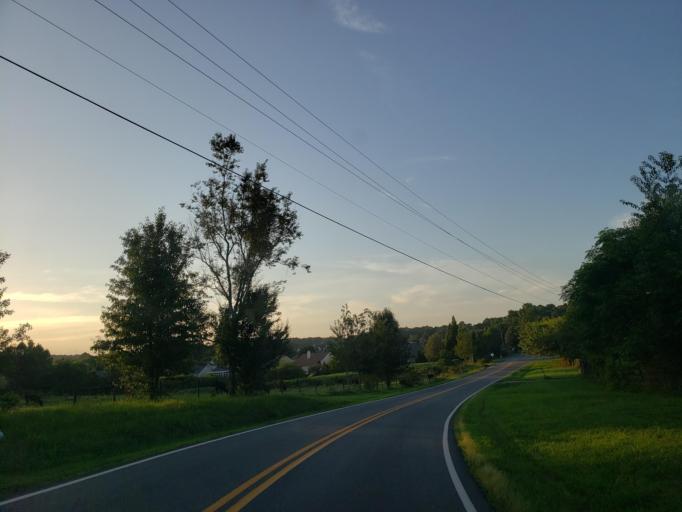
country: US
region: Georgia
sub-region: Forsyth County
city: Cumming
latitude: 34.2297
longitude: -84.2142
